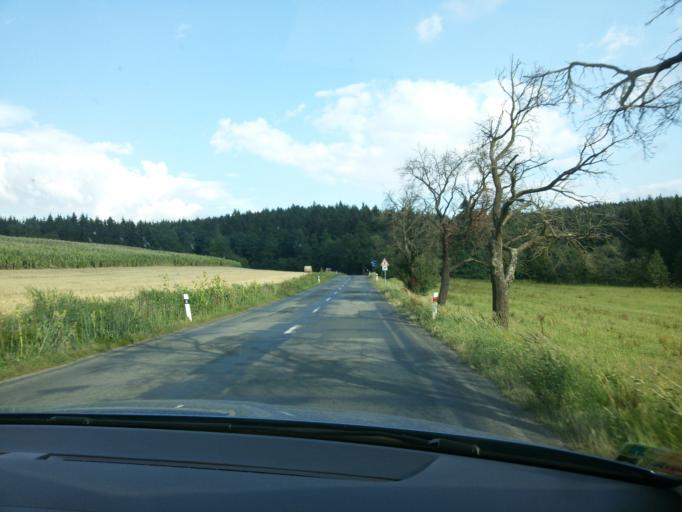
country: CZ
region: South Moravian
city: Olesnice
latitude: 49.5373
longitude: 16.4481
